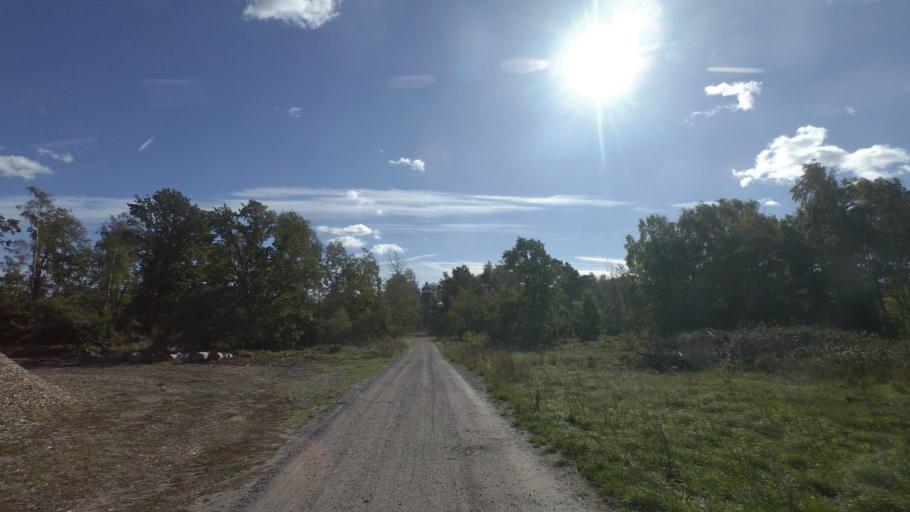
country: DK
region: Capital Region
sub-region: Bornholm Kommune
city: Nexo
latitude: 55.0042
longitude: 15.0871
